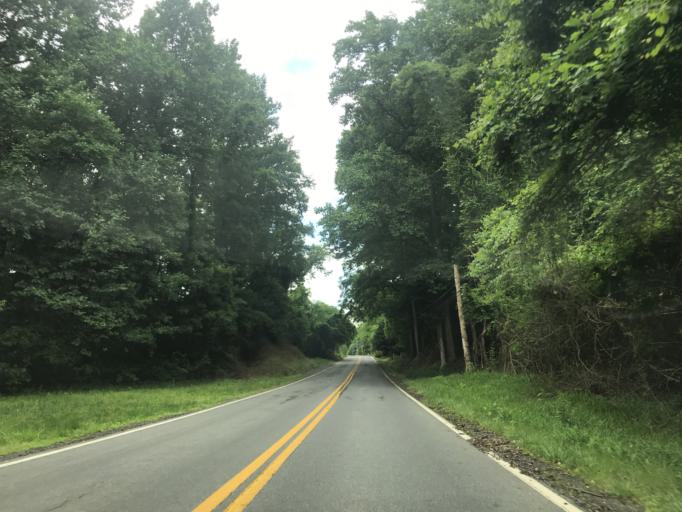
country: US
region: Maryland
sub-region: Caroline County
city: Ridgely
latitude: 38.8907
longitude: -75.9602
